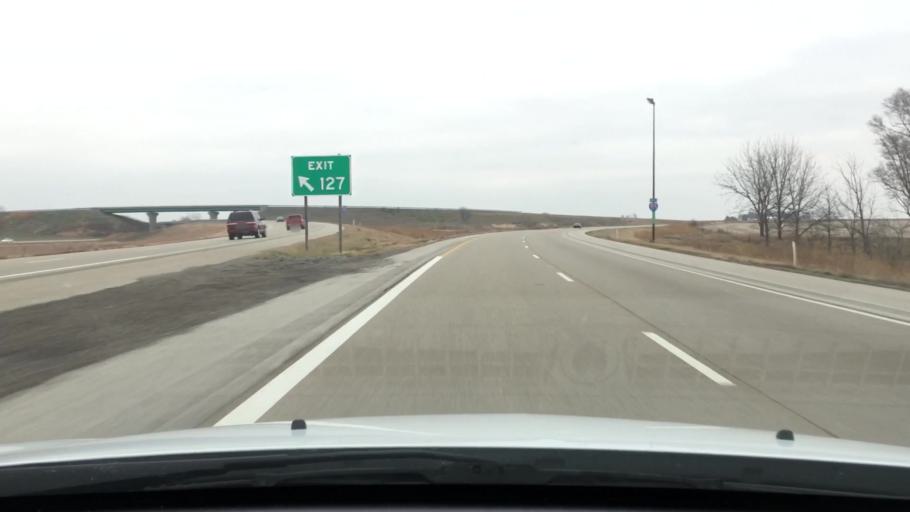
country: US
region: Illinois
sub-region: Logan County
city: Lincoln
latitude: 40.1744
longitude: -89.4162
